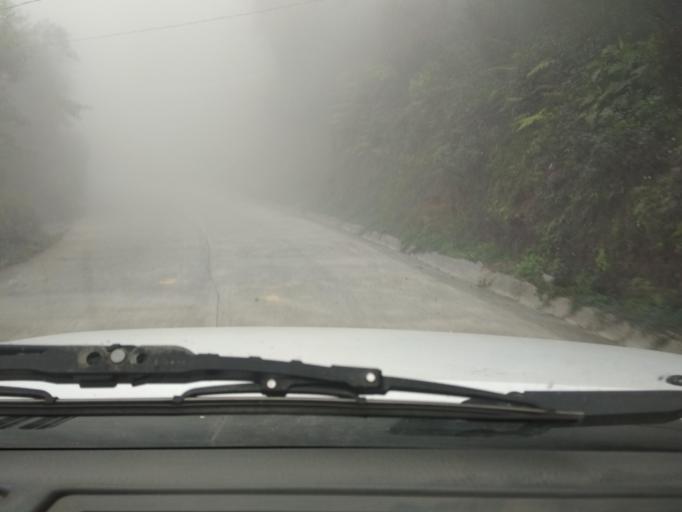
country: MX
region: Veracruz
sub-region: La Perla
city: Barrio de San Miguel
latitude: 18.9449
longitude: -97.1206
